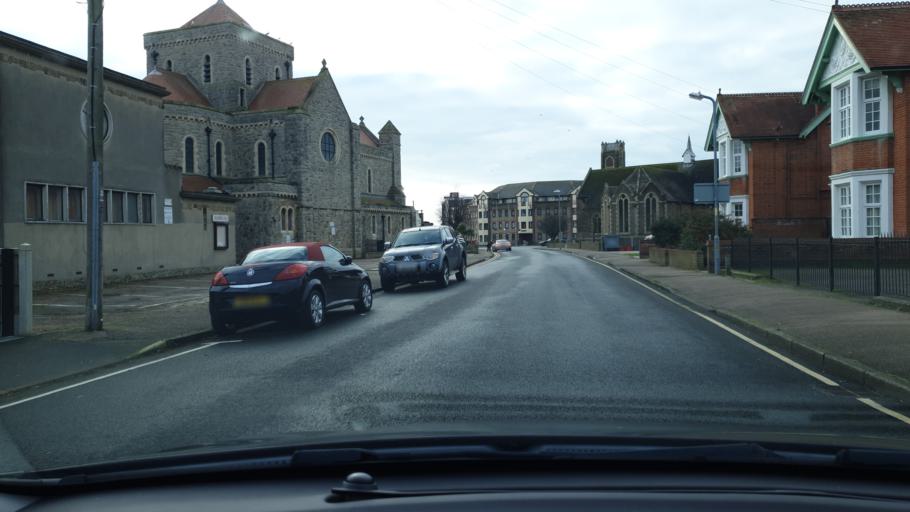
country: GB
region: England
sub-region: Essex
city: Clacton-on-Sea
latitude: 51.7908
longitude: 1.1584
